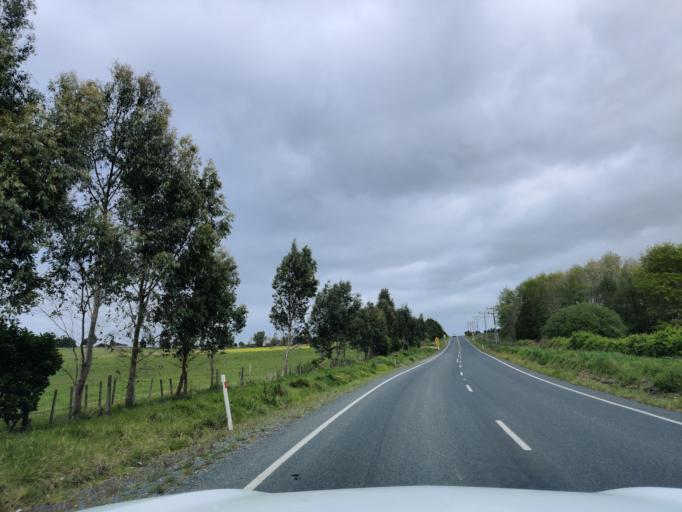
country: NZ
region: Waikato
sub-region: Waikato District
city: Ngaruawahia
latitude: -37.5775
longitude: 175.1391
